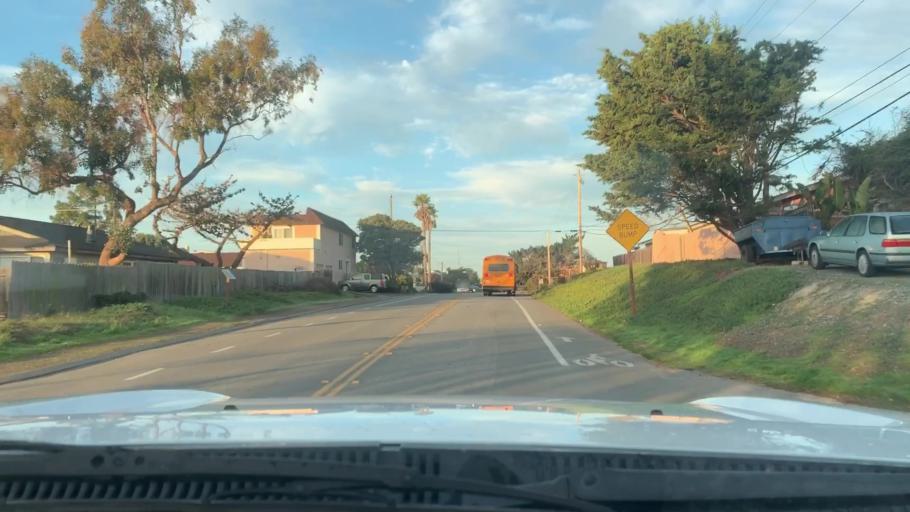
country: US
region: California
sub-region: San Luis Obispo County
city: Los Osos
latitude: 35.3300
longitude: -120.8255
